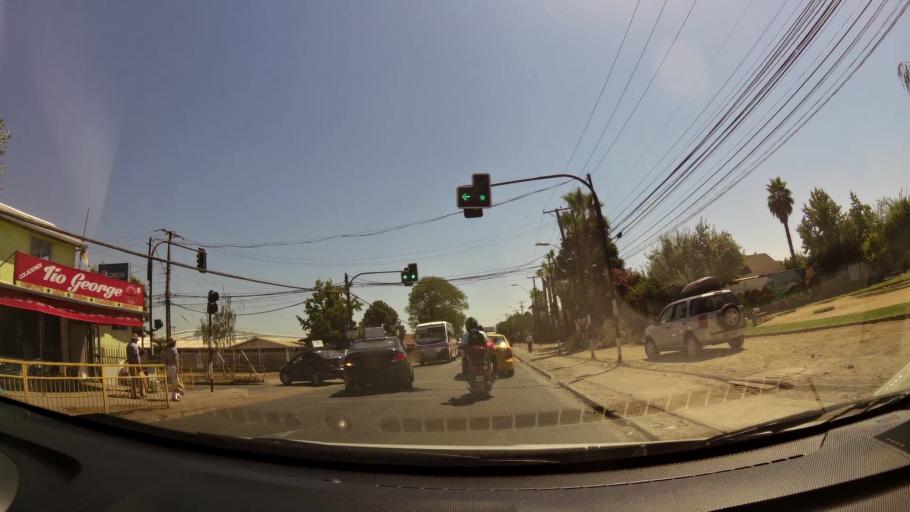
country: CL
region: Maule
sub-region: Provincia de Curico
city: Curico
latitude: -34.9671
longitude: -71.2300
